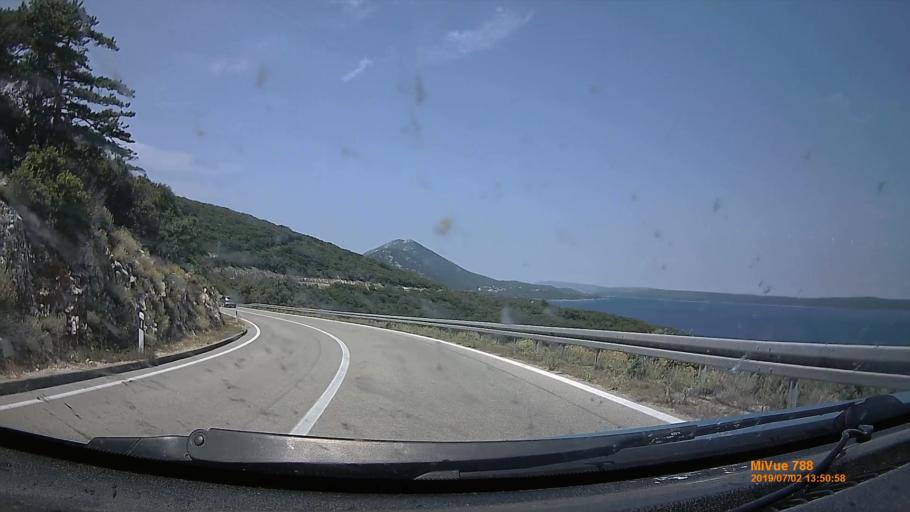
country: HR
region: Primorsko-Goranska
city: Mali Losinj
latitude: 44.6009
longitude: 14.4066
